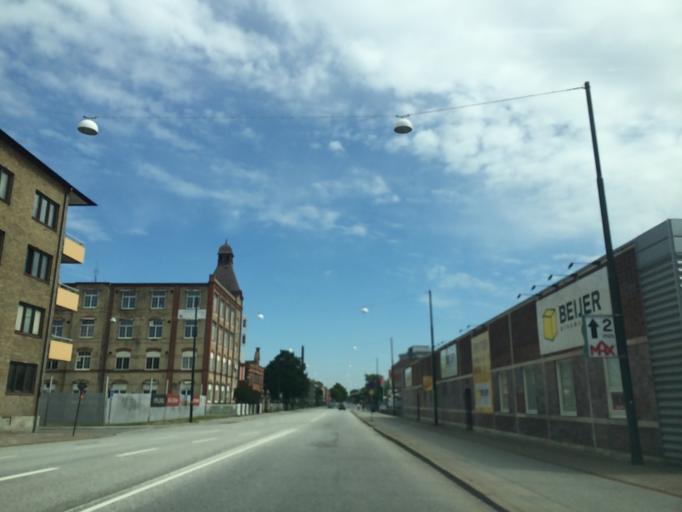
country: SE
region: Skane
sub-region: Malmo
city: Malmoe
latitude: 55.5834
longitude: 13.0092
